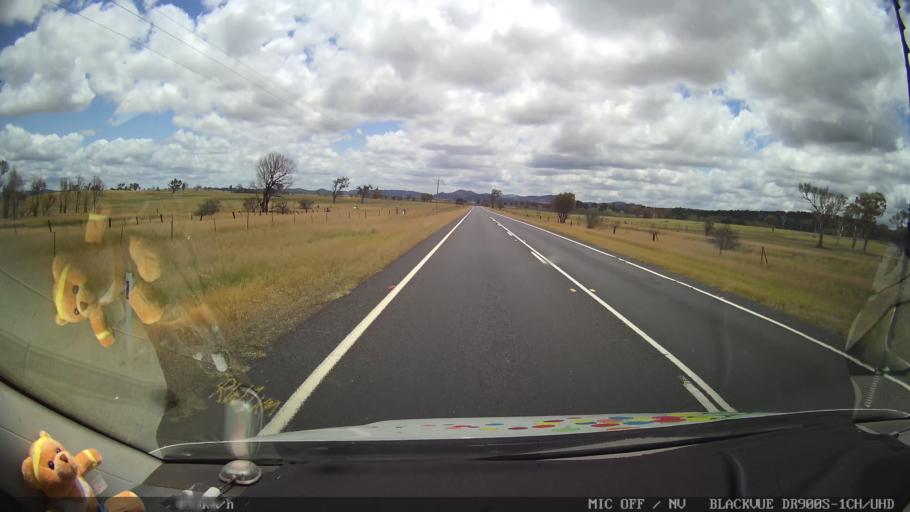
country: AU
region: New South Wales
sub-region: Glen Innes Severn
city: Glen Innes
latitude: -29.4272
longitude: 151.8574
